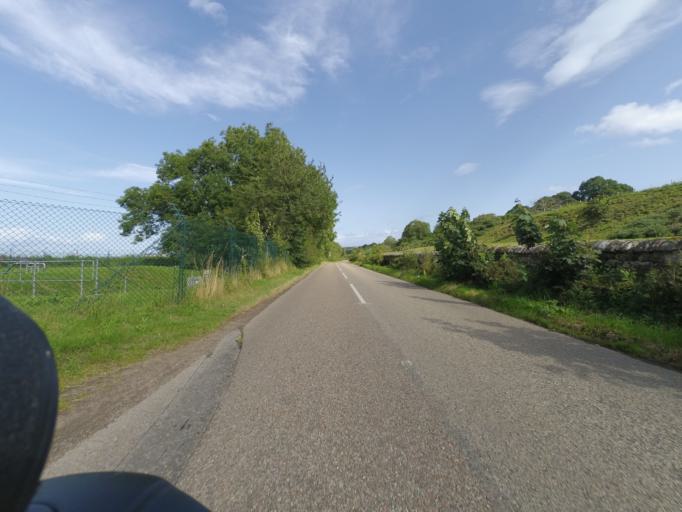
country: GB
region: Scotland
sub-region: Highland
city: Invergordon
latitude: 57.6585
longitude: -4.1431
